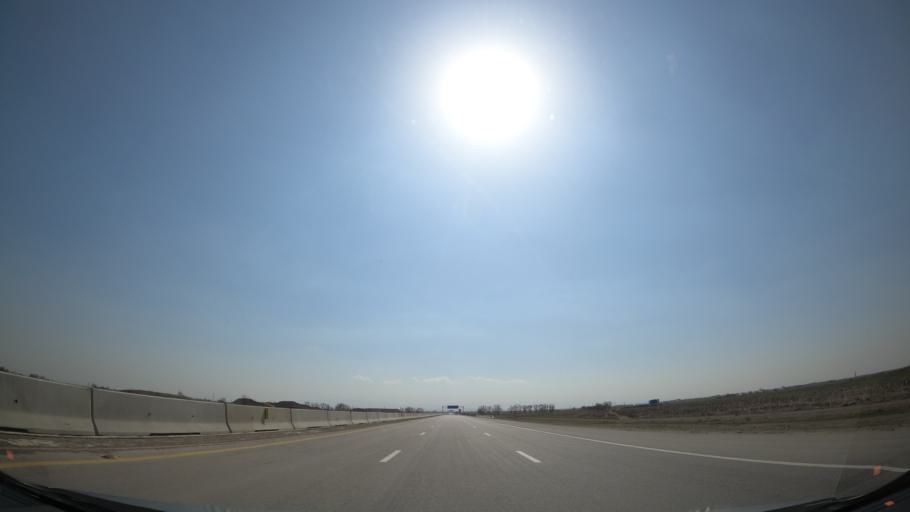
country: IR
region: Qazvin
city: Abyek
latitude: 35.9832
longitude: 50.4617
